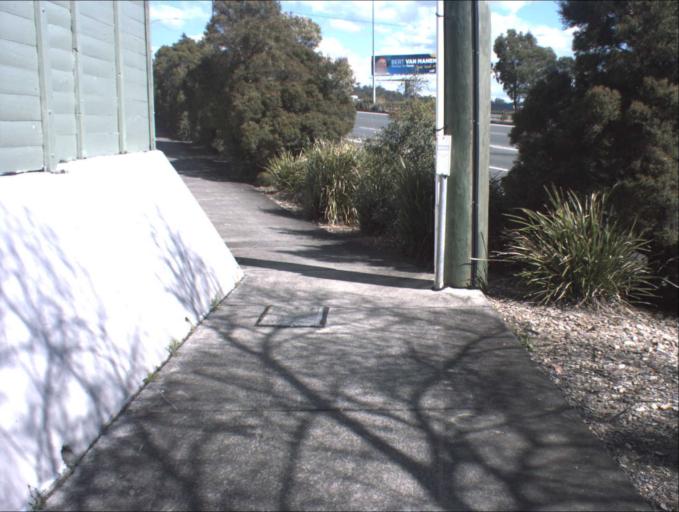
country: AU
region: Queensland
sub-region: Logan
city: Waterford West
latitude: -27.6981
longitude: 153.1573
